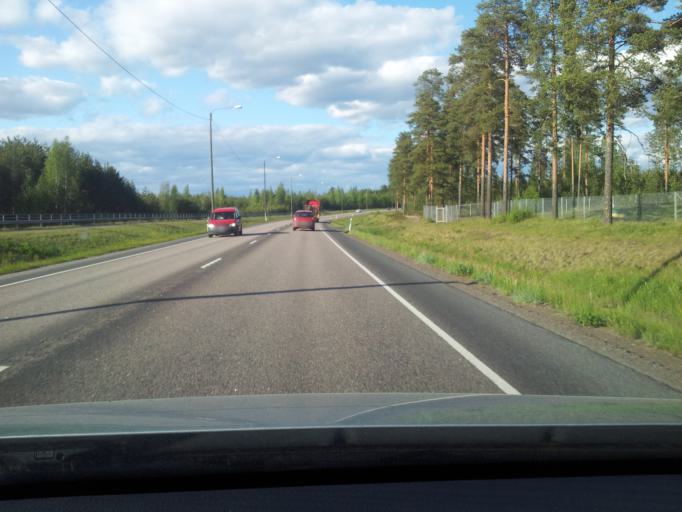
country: FI
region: Kymenlaakso
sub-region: Kouvola
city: Kouvola
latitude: 60.9016
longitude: 26.9204
